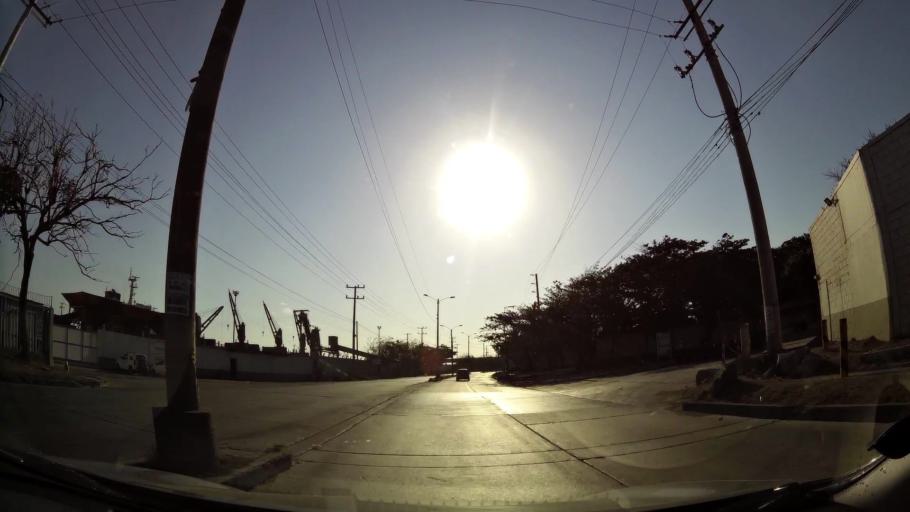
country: CO
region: Atlantico
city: Barranquilla
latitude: 11.0376
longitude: -74.8180
